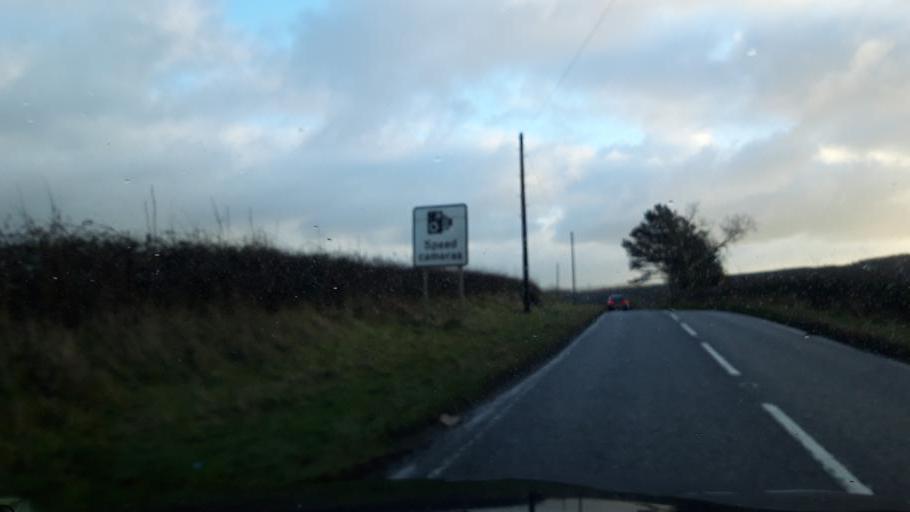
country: GB
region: Northern Ireland
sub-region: Moyle District
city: Ballycastle
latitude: 55.1907
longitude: -6.2761
